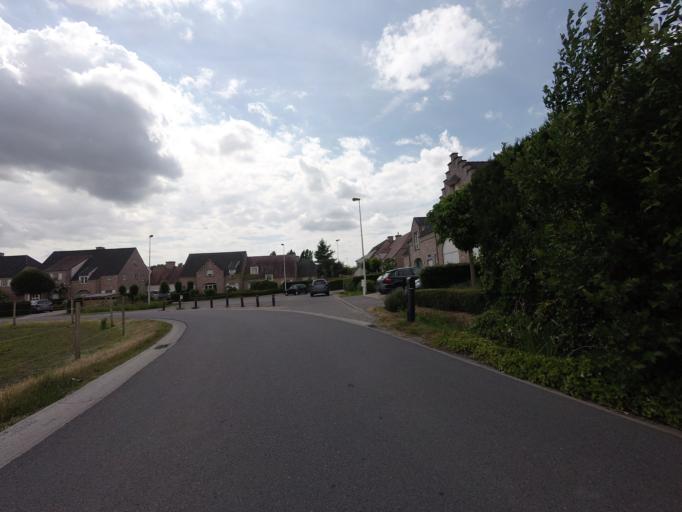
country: BE
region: Flanders
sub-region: Provincie Antwerpen
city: Hove
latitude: 51.1372
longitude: 4.4689
